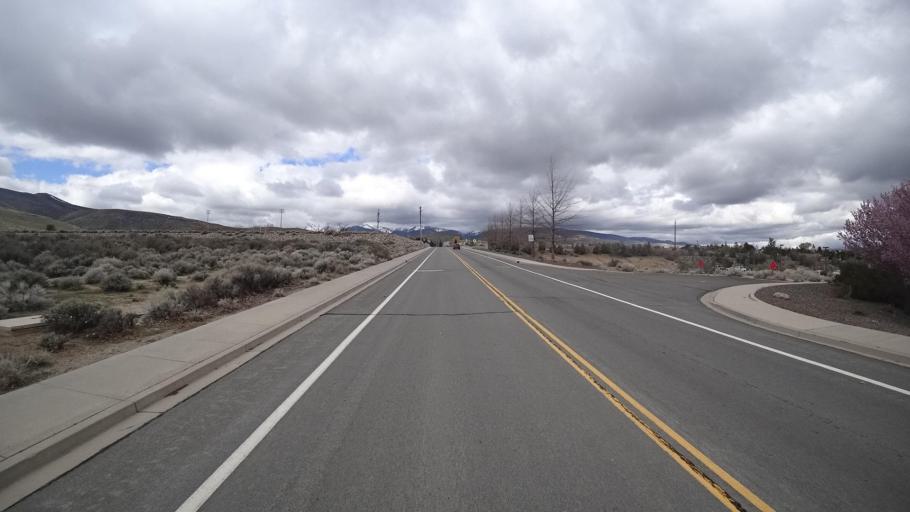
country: US
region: Nevada
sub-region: Storey County
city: Virginia City
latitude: 39.3890
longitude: -119.7705
